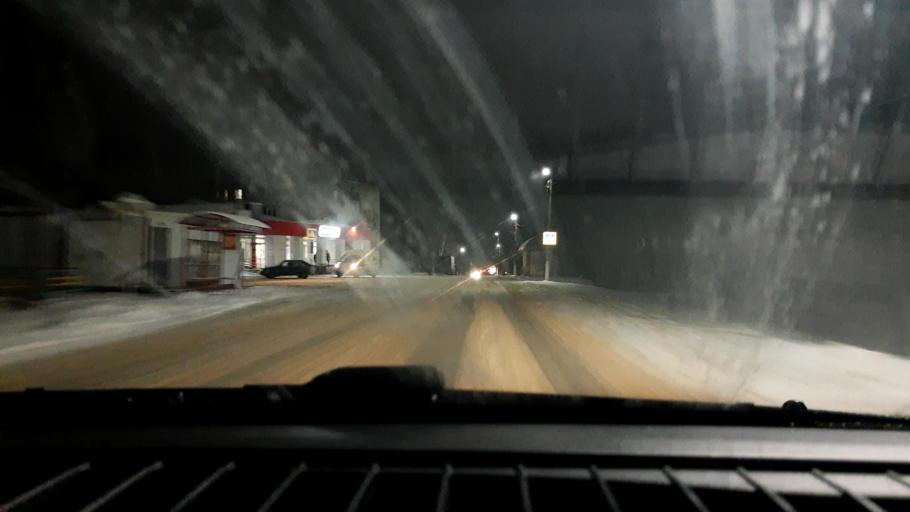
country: RU
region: Nizjnij Novgorod
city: Bogorodsk
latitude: 56.0951
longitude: 43.5393
